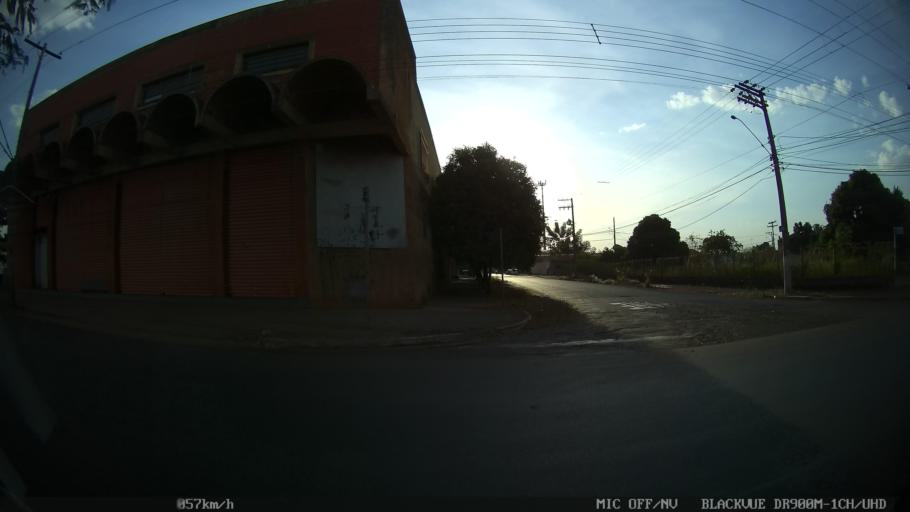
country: BR
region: Sao Paulo
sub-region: Ribeirao Preto
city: Ribeirao Preto
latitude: -21.1337
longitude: -47.7956
